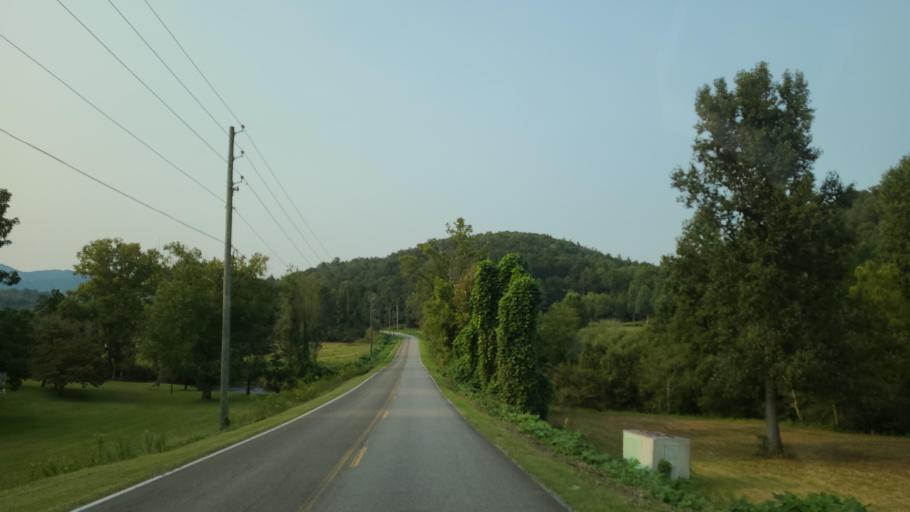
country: US
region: Georgia
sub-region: Gilmer County
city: Ellijay
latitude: 34.7719
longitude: -84.4196
